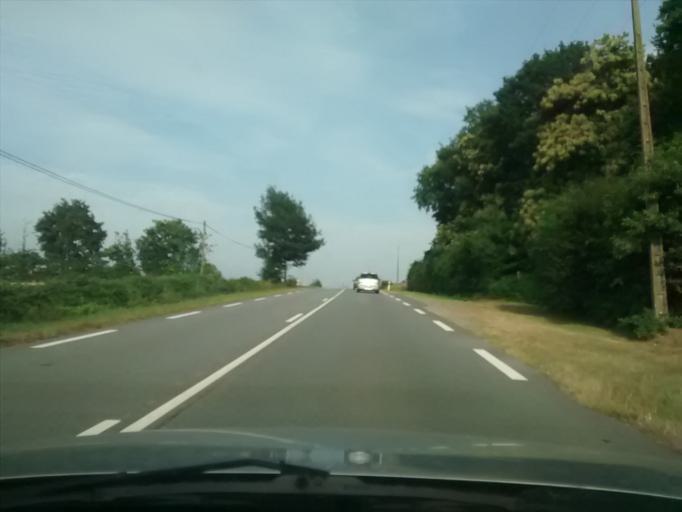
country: FR
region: Brittany
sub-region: Departement d'Ille-et-Vilaine
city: Erbree
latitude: 48.1172
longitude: -1.1522
